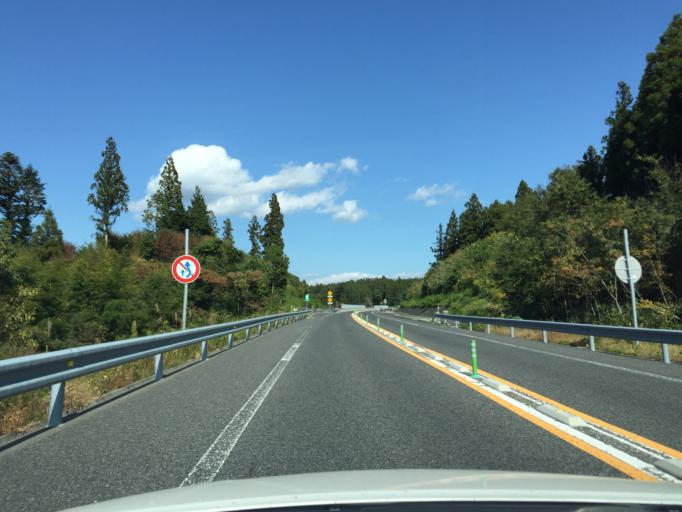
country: JP
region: Fukushima
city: Funehikimachi-funehiki
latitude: 37.2888
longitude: 140.6054
